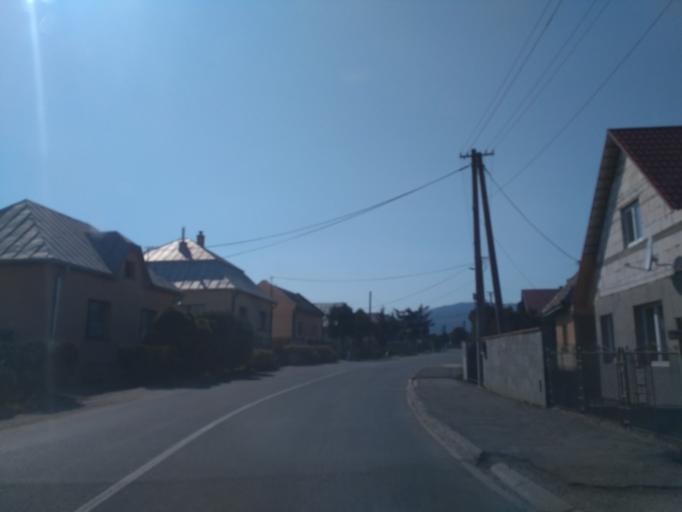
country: SK
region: Kosicky
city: Secovce
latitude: 48.6992
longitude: 21.6438
